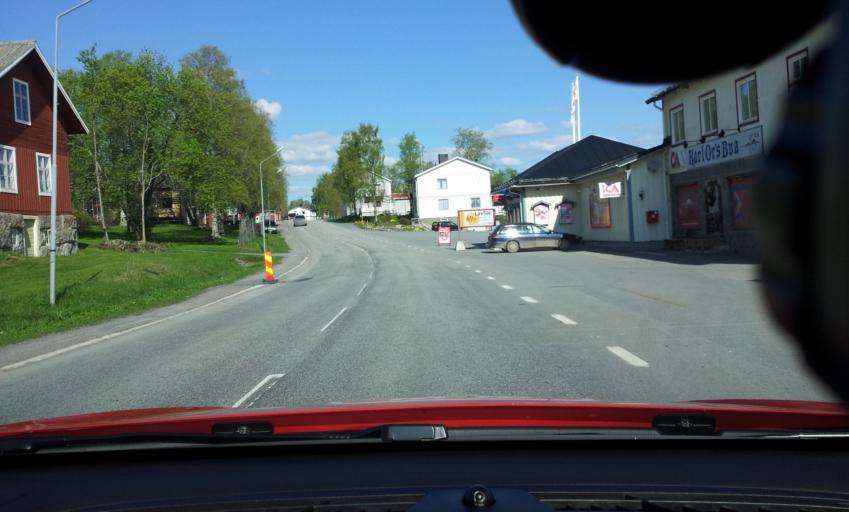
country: SE
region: Jaemtland
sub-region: Krokoms Kommun
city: Krokom
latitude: 63.1744
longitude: 14.0978
